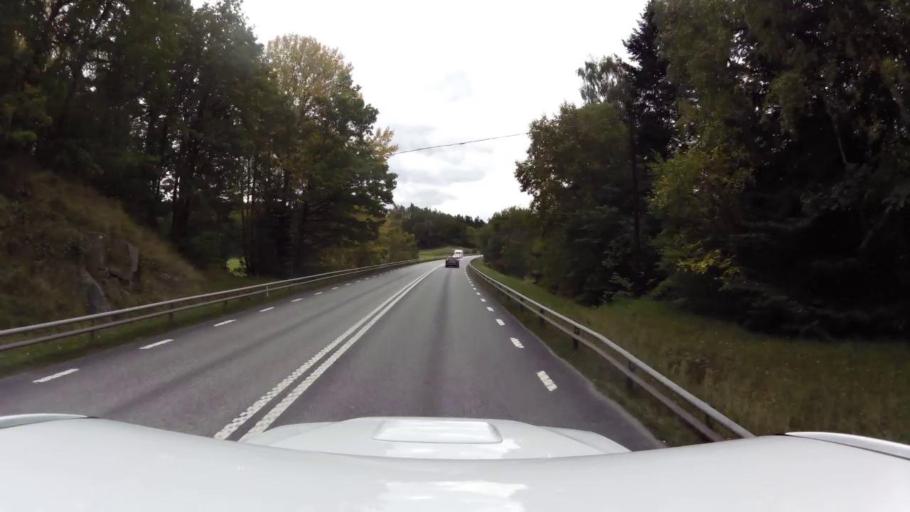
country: SE
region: OEstergoetland
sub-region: Kinda Kommun
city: Rimforsa
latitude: 58.1834
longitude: 15.6711
